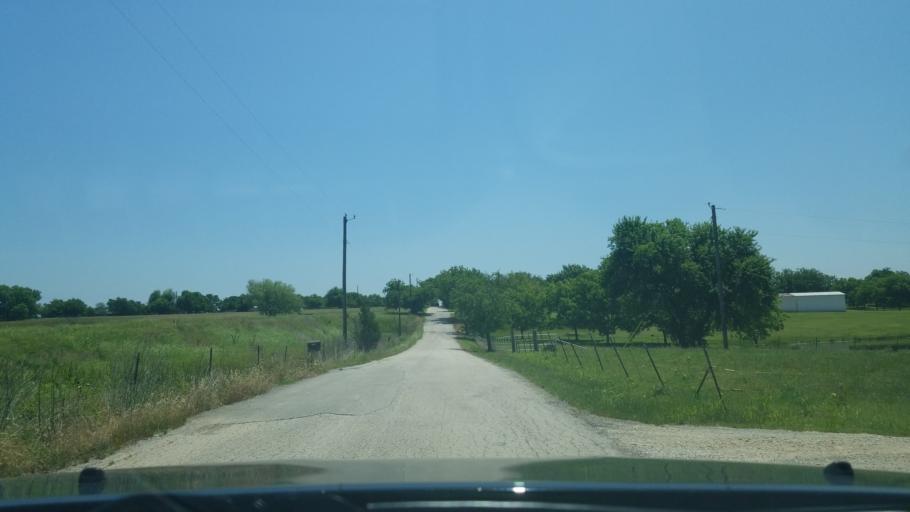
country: US
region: Texas
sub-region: Denton County
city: Sanger
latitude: 33.3505
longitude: -97.2089
